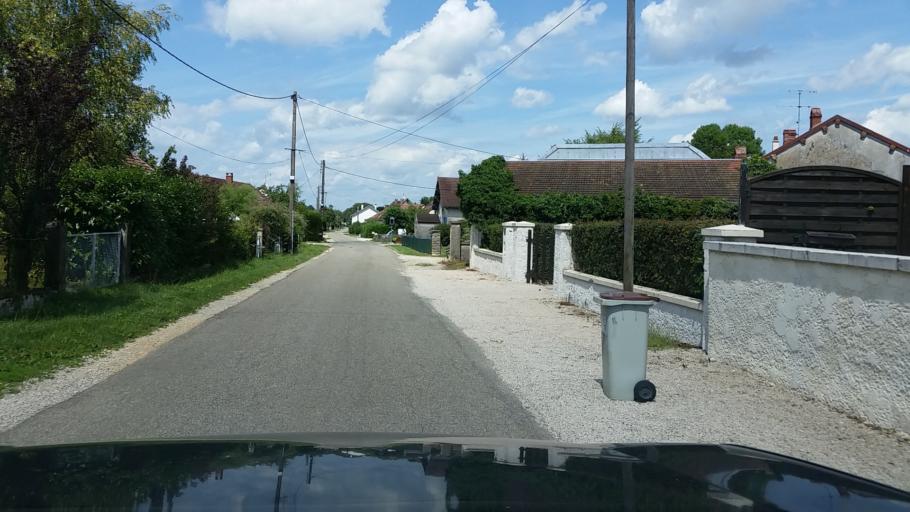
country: FR
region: Franche-Comte
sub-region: Departement du Jura
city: Bletterans
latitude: 46.7848
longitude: 5.5077
